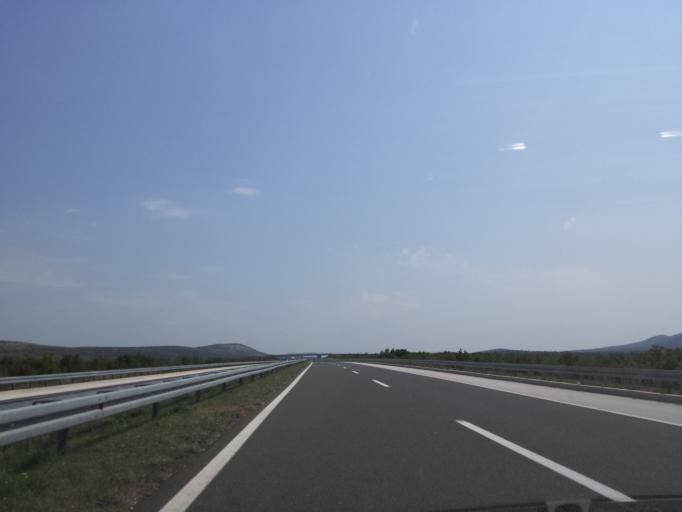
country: HR
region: Zadarska
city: Benkovac
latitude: 43.9587
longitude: 15.6682
